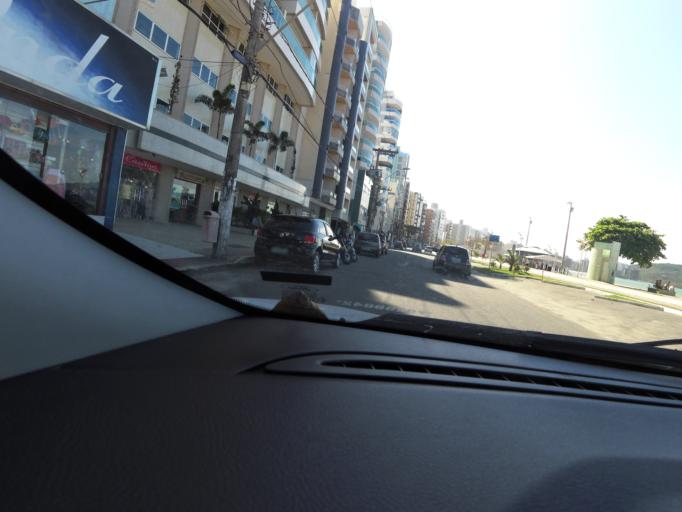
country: BR
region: Espirito Santo
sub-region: Guarapari
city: Guarapari
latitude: -20.6537
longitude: -40.4864
